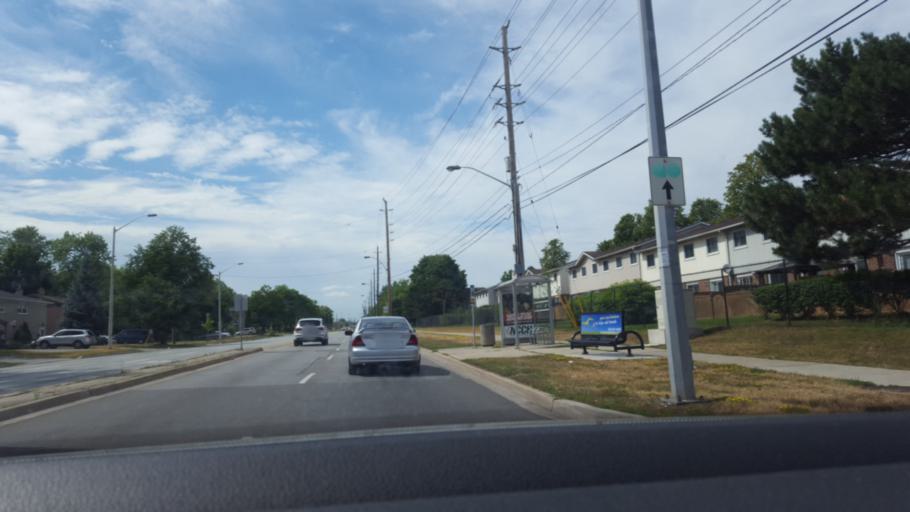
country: CA
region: Ontario
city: Burlington
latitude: 43.3693
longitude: -79.7562
